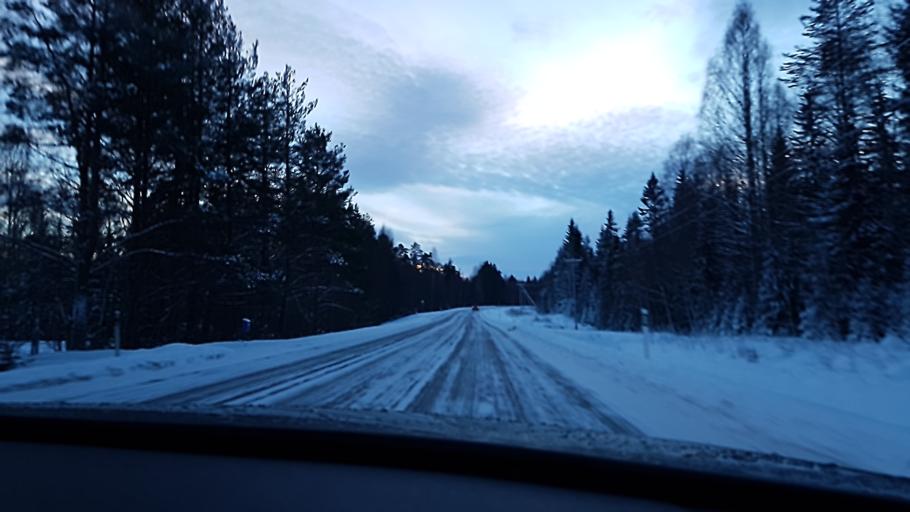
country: SE
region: Jaemtland
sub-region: Harjedalens Kommun
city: Sveg
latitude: 62.0768
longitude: 14.9434
